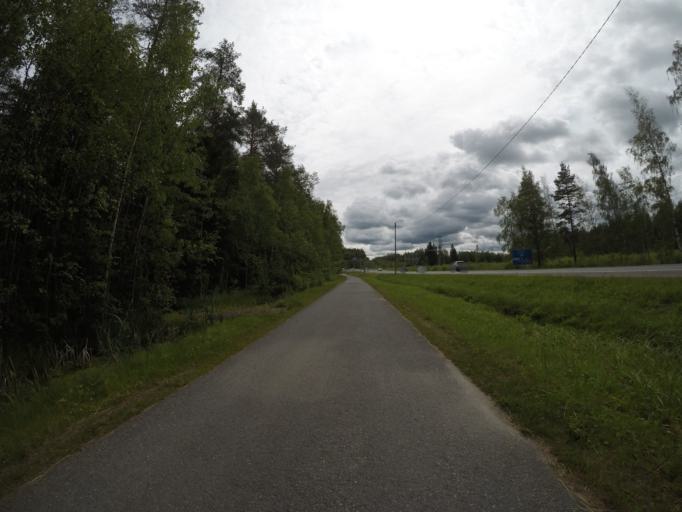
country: FI
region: Haeme
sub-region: Haemeenlinna
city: Haemeenlinna
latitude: 60.9864
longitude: 24.5046
